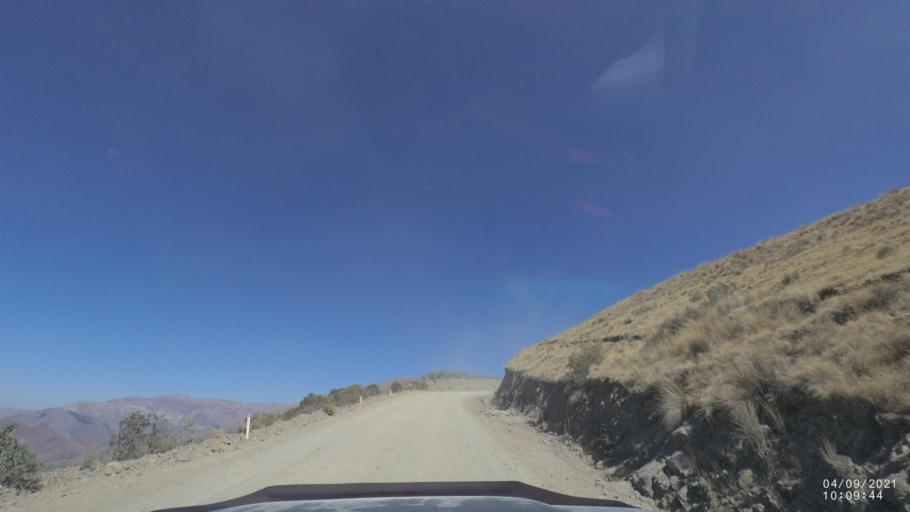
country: BO
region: Cochabamba
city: Sipe Sipe
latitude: -17.3443
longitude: -66.3946
